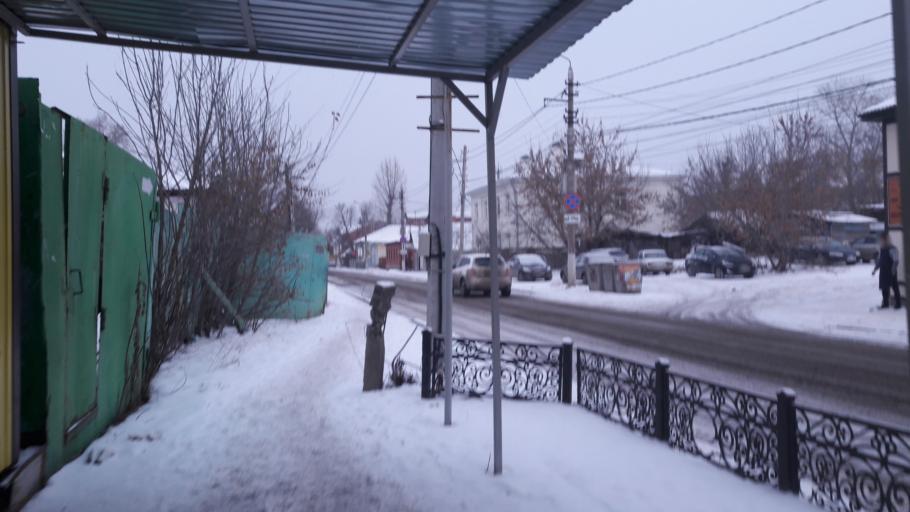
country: RU
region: Tula
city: Tula
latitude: 54.1873
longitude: 37.6170
